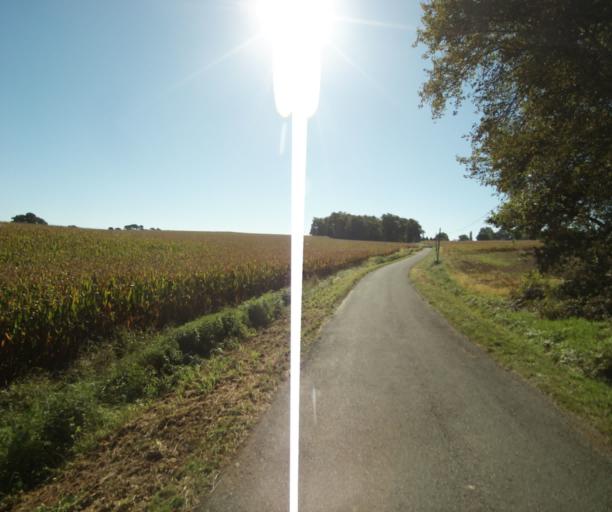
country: FR
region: Midi-Pyrenees
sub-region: Departement du Gers
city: Eauze
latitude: 43.8081
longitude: 0.1293
